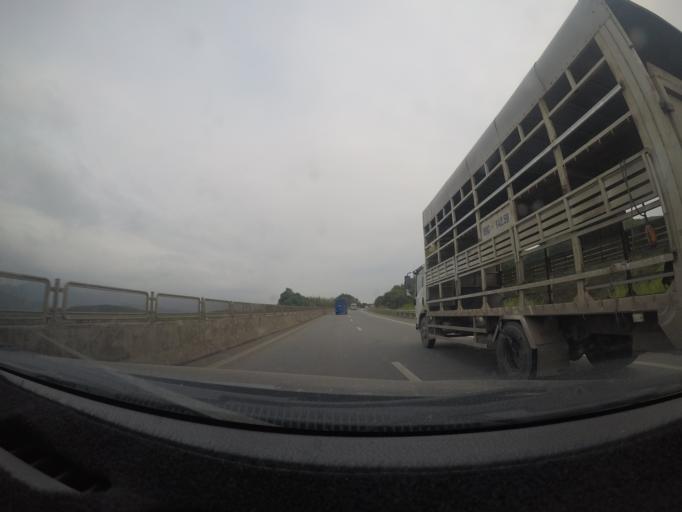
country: VN
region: Yen Bai
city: Thi Tran Yen The
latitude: 21.9410
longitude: 104.5865
